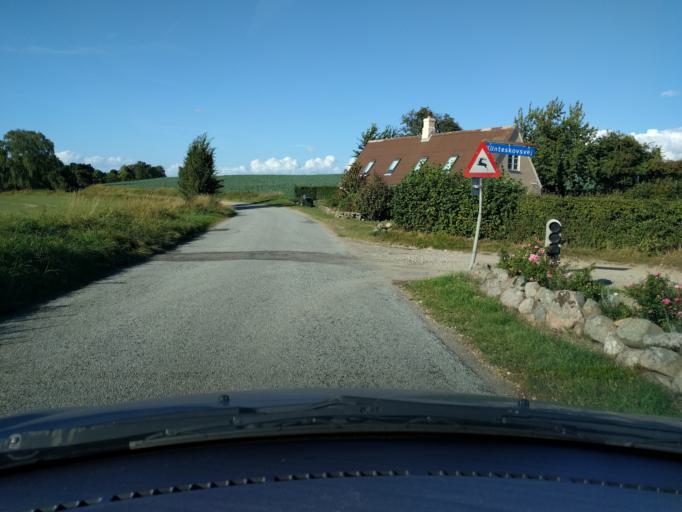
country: DK
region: South Denmark
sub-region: Assens Kommune
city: Harby
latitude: 55.1375
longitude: 10.0264
